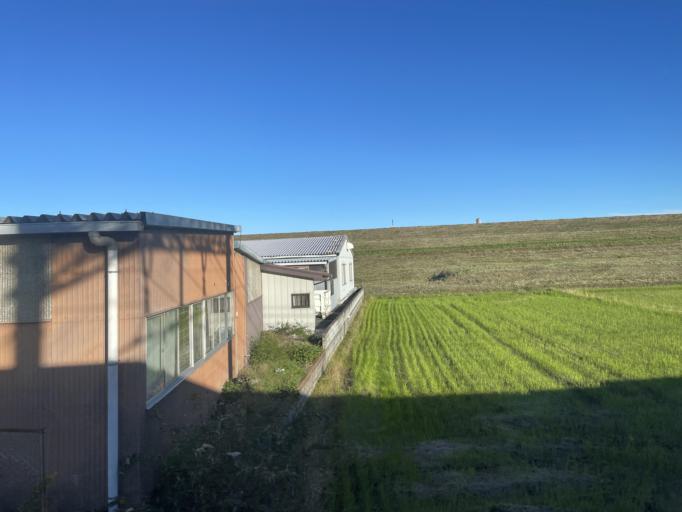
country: JP
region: Ibaraki
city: Koga
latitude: 36.1831
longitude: 139.6877
